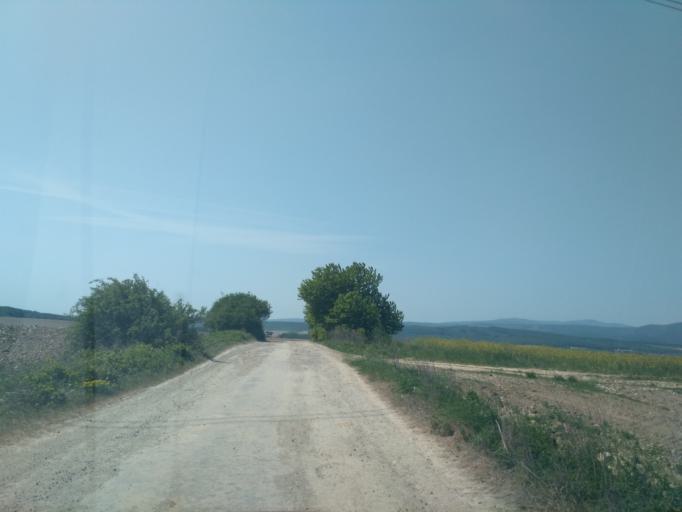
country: SK
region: Kosicky
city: Kosice
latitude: 48.7943
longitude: 21.3743
